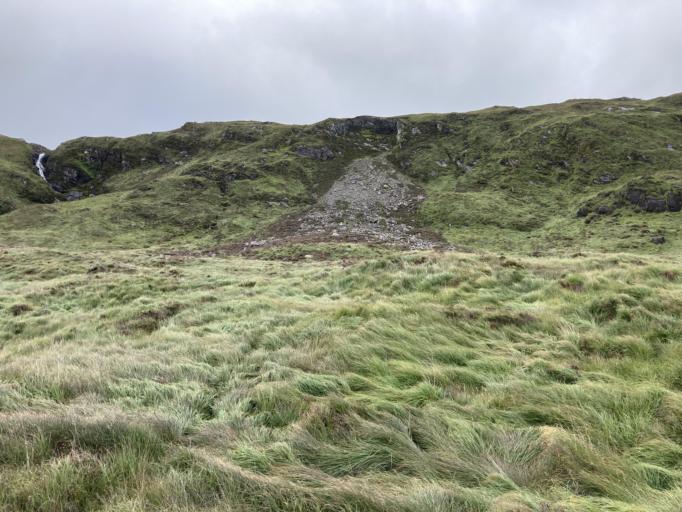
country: GB
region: Scotland
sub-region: Highland
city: Isle of Skye
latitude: 57.0151
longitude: -6.3190
